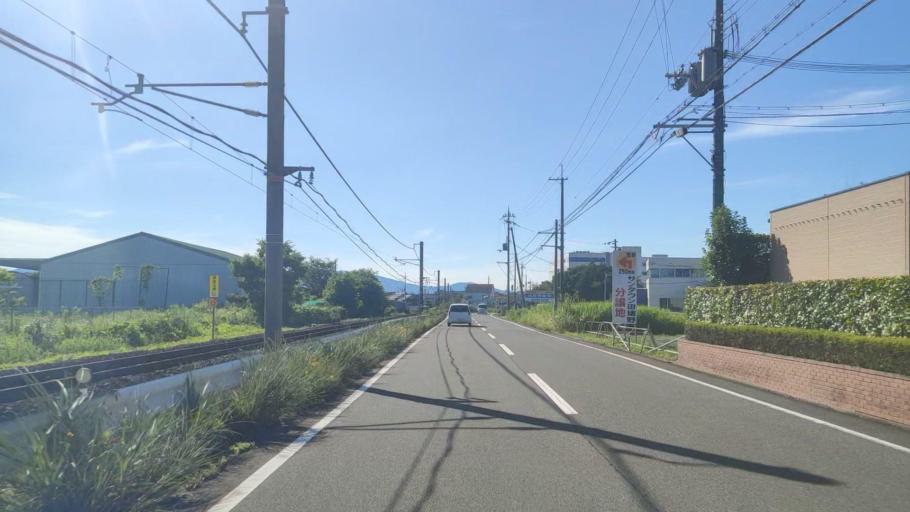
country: JP
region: Shiga Prefecture
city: Minakuchicho-matoba
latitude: 34.8977
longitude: 136.2183
